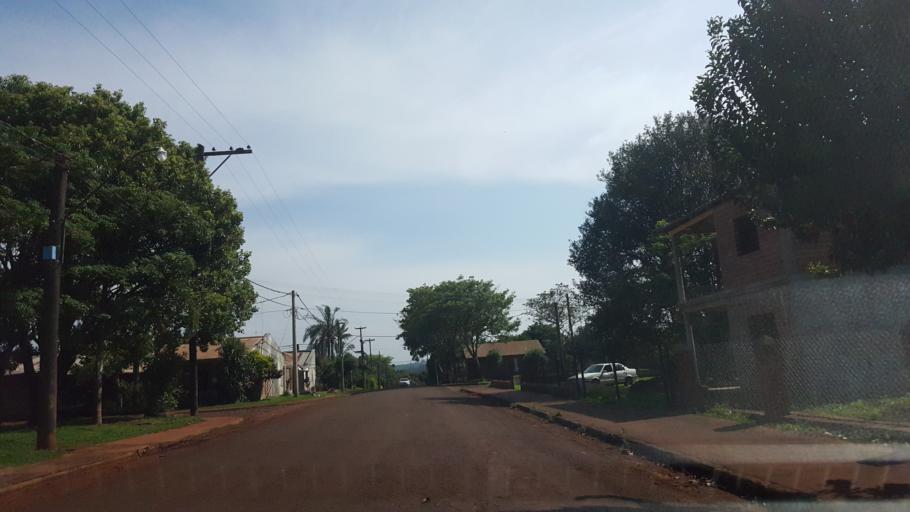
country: AR
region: Misiones
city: Capiovi
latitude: -26.9344
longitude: -55.0555
